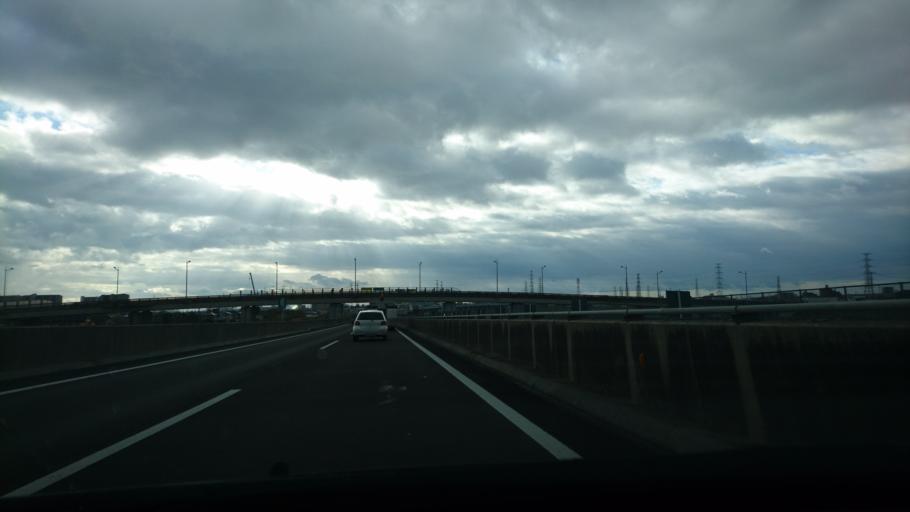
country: JP
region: Miyagi
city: Rifu
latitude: 38.2948
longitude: 140.9887
